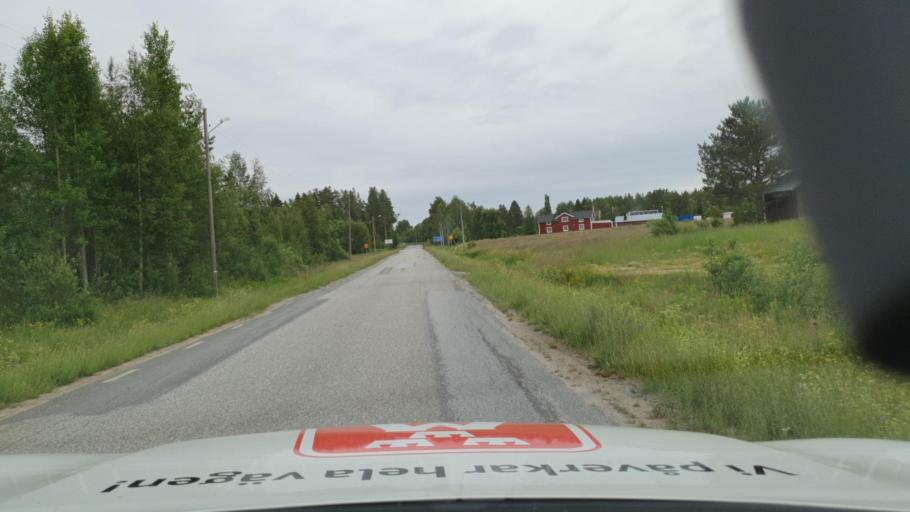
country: SE
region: Vaesterbotten
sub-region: Nordmalings Kommun
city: Nordmaling
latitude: 63.5384
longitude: 19.3970
